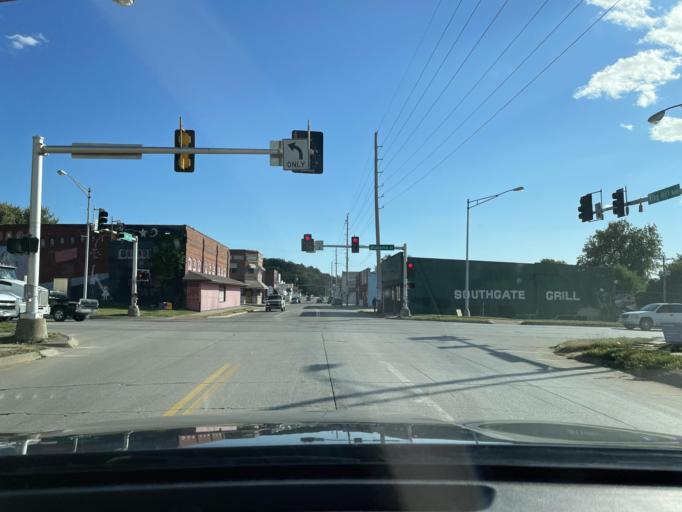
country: US
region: Kansas
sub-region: Doniphan County
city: Elwood
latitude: 39.7124
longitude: -94.8623
